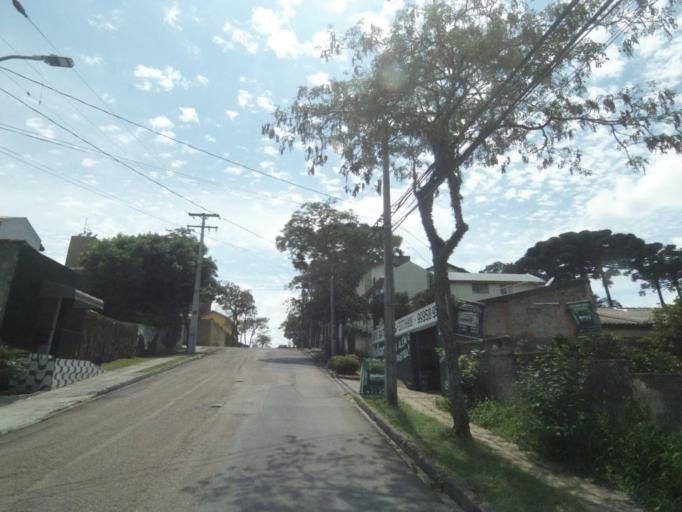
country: BR
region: Parana
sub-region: Curitiba
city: Curitiba
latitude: -25.4587
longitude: -49.3501
